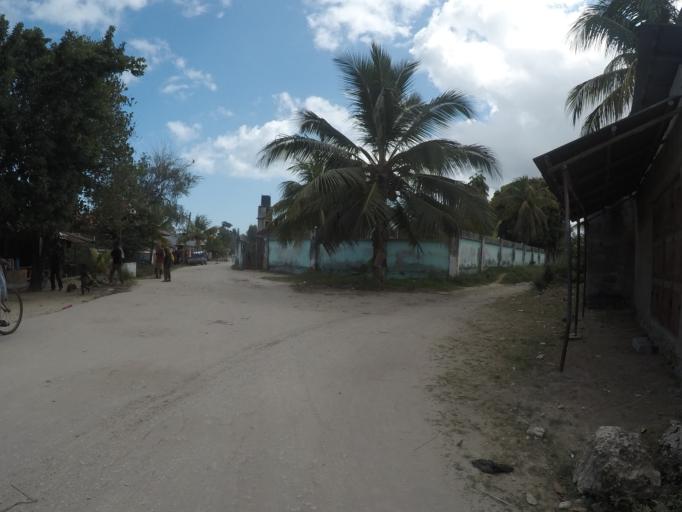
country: TZ
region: Zanzibar Urban/West
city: Zanzibar
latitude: -6.1845
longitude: 39.2116
